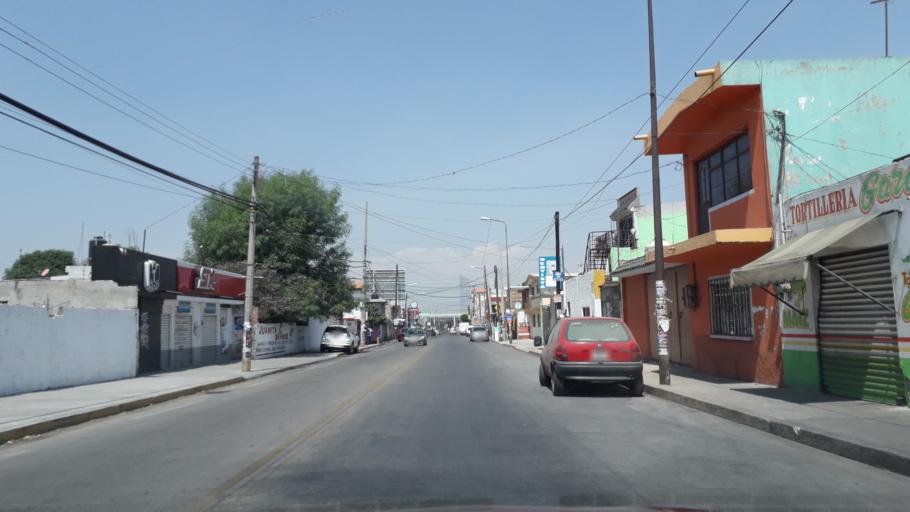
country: MX
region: Puebla
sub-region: Cuautlancingo
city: Sanctorum
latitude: 19.0899
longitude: -98.2260
